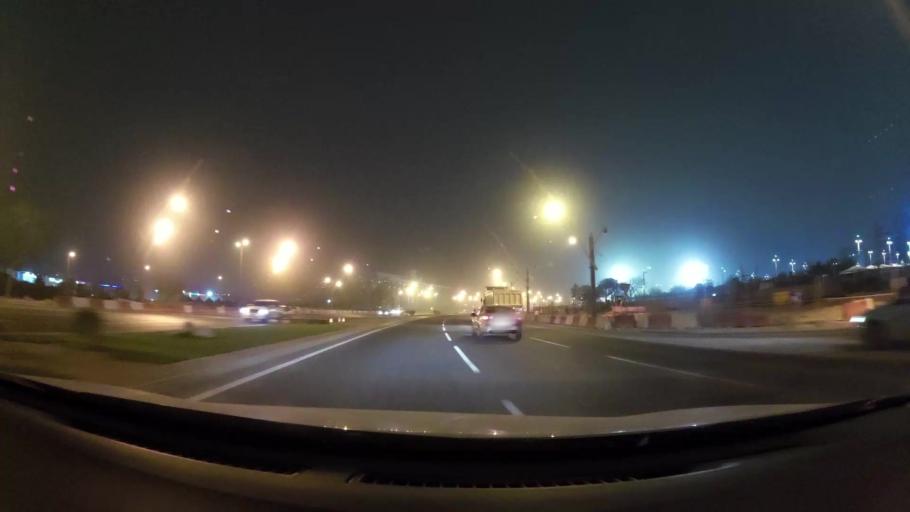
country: QA
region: Baladiyat ar Rayyan
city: Ar Rayyan
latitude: 25.2675
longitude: 51.4497
